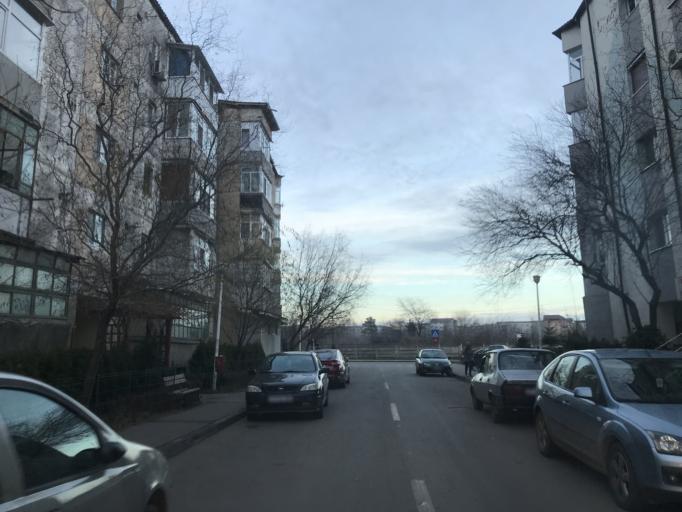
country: RO
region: Olt
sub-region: Municipiul Slatina
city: Slatina
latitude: 44.4261
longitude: 24.3811
